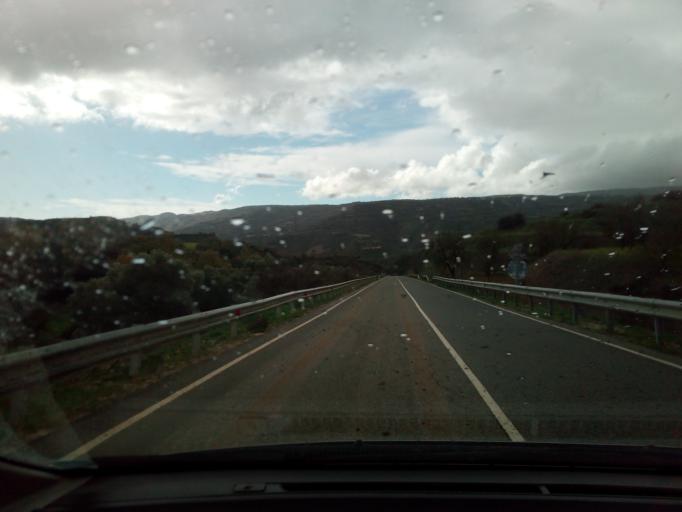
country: CY
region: Pafos
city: Polis
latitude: 34.9583
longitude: 32.4747
